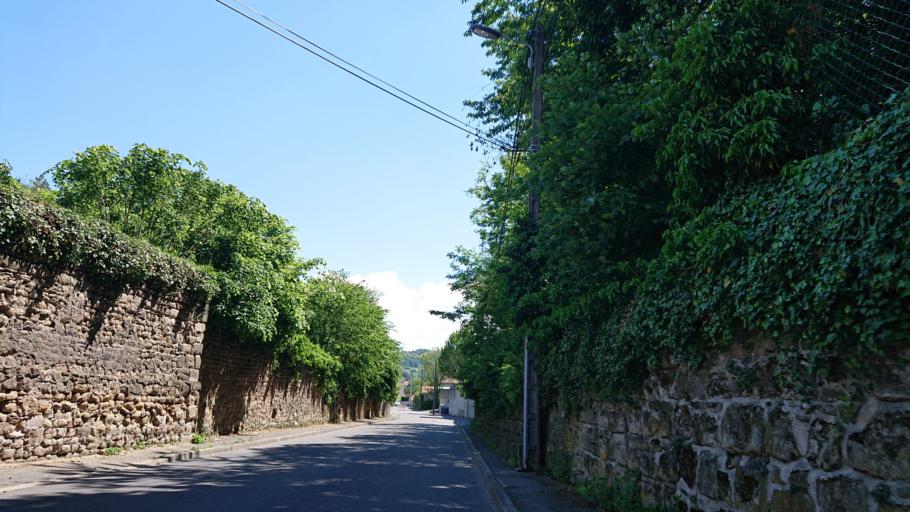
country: FR
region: Rhone-Alpes
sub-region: Departement de la Loire
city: Villars
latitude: 45.4488
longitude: 4.3605
